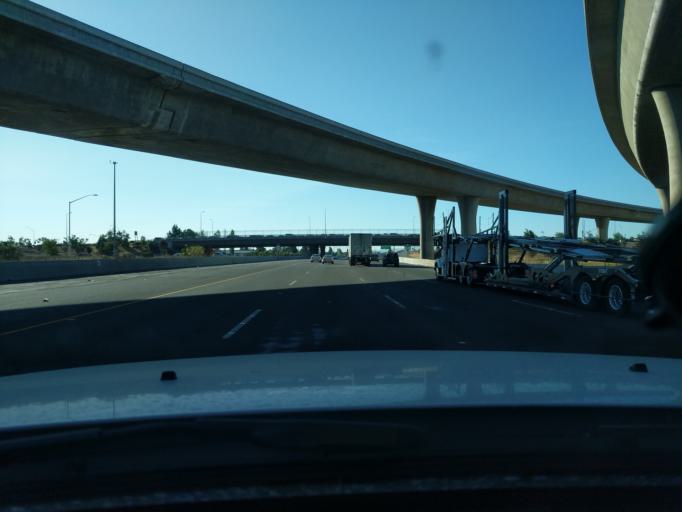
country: US
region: California
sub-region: Santa Clara County
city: Milpitas
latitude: 37.4273
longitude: -121.9175
